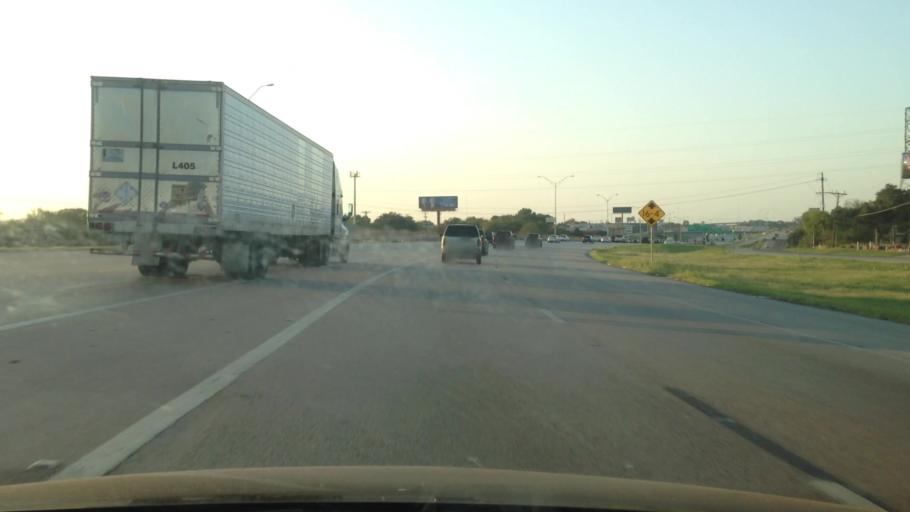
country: US
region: Texas
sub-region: Tarrant County
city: Forest Hill
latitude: 32.6727
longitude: -97.2401
